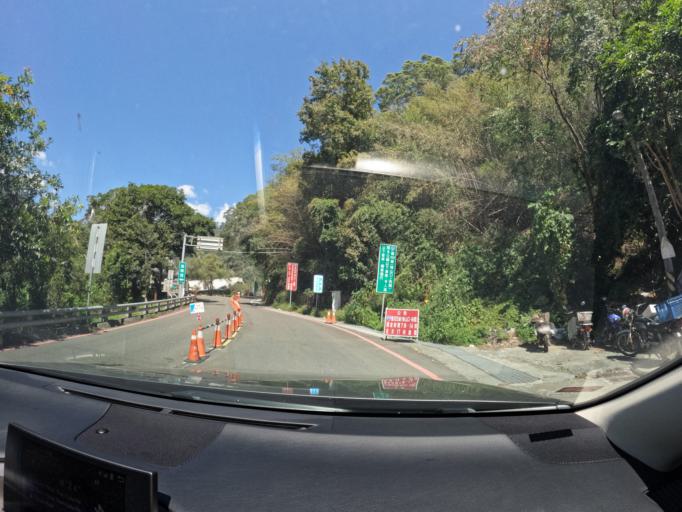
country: TW
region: Taiwan
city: Yujing
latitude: 23.2650
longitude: 120.8259
